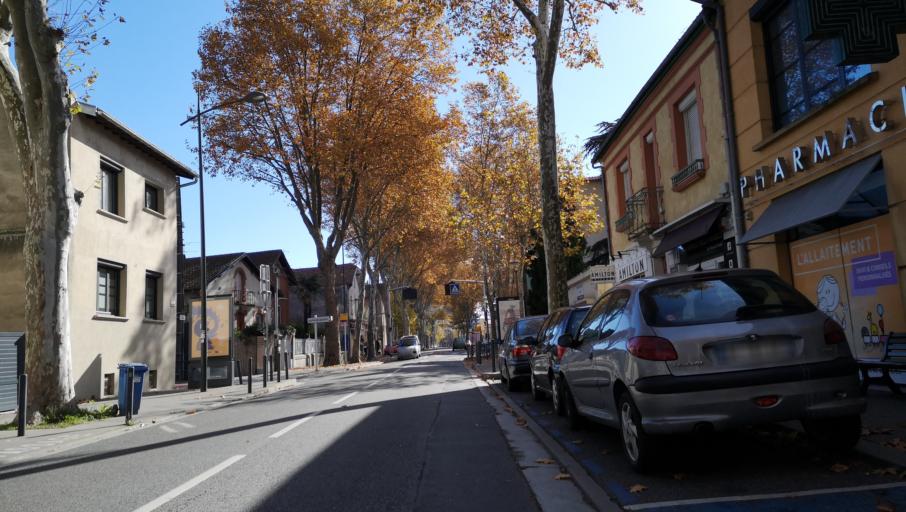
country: FR
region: Midi-Pyrenees
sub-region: Departement de la Haute-Garonne
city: Blagnac
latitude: 43.6148
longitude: 1.4107
